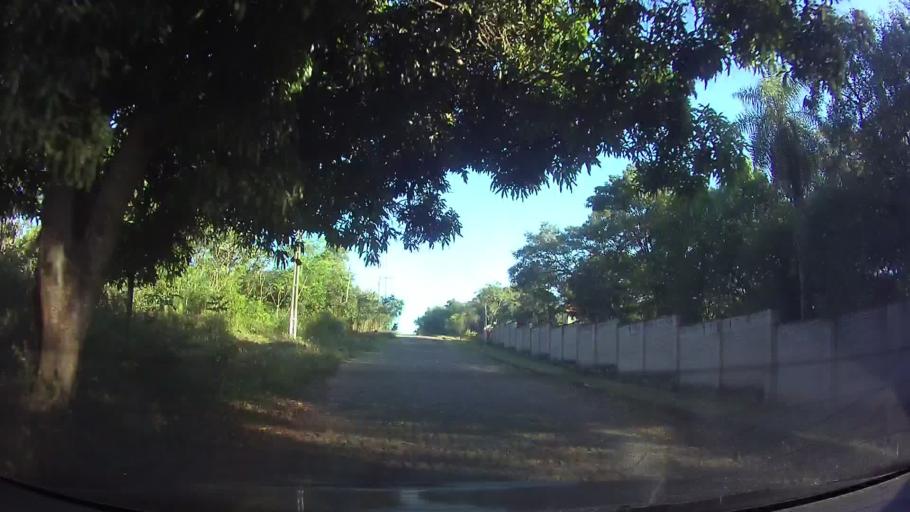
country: PY
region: Cordillera
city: San Bernardino
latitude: -25.3117
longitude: -57.2651
